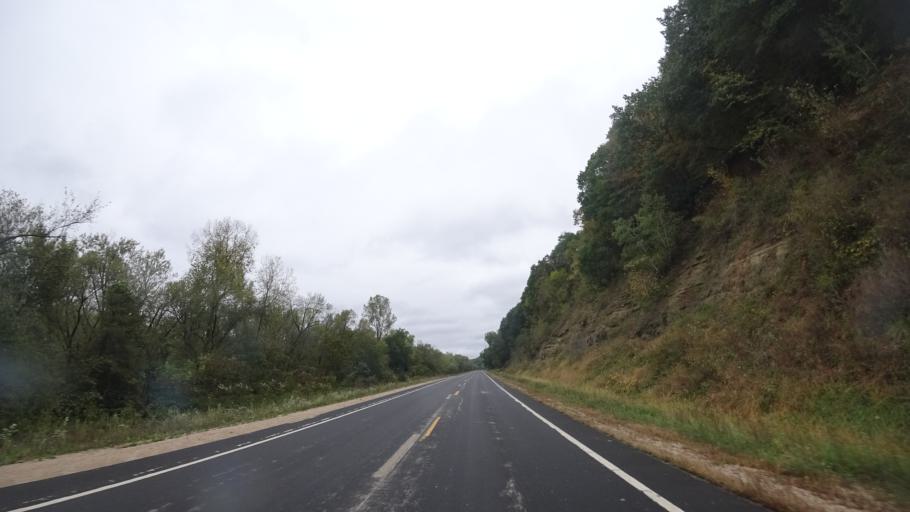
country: US
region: Wisconsin
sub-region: Grant County
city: Boscobel
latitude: 43.1835
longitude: -90.6758
